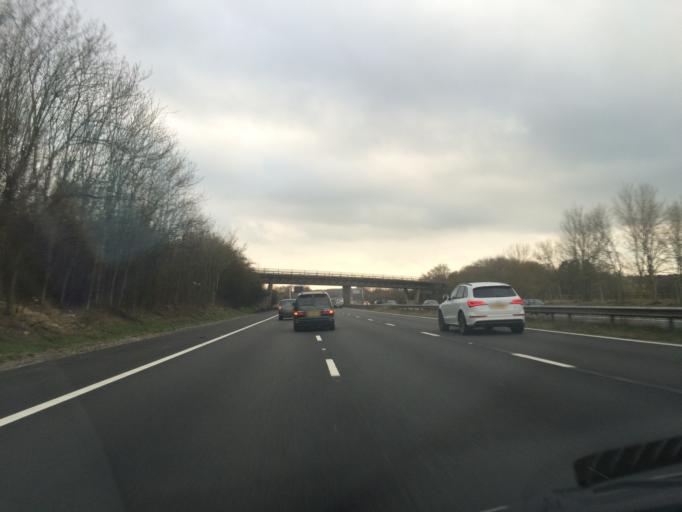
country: GB
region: England
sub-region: West Berkshire
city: Wickham
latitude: 51.4469
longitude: -1.4447
